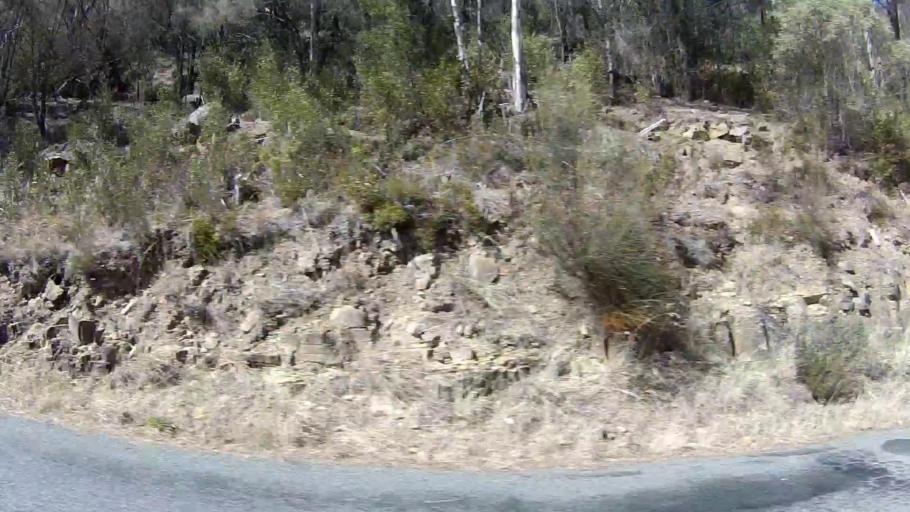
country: AU
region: Tasmania
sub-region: Sorell
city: Sorell
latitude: -42.5655
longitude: 147.8245
